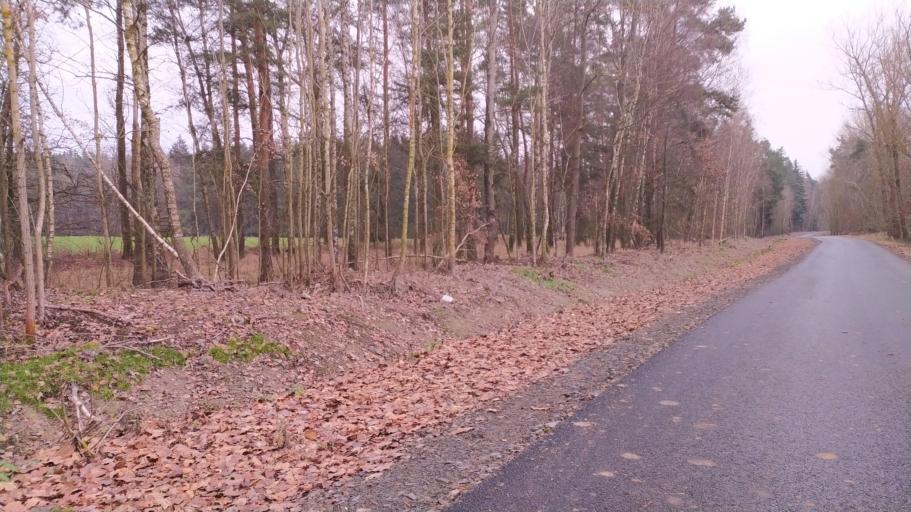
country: DE
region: Bavaria
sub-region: Upper Franconia
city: Schirnding
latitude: 50.1010
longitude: 12.2707
